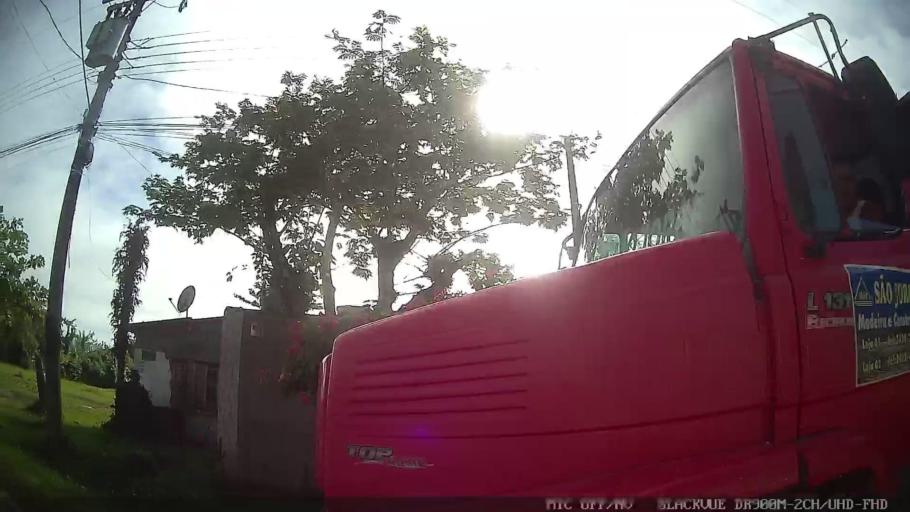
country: BR
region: Sao Paulo
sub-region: Peruibe
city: Peruibe
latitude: -24.2327
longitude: -46.9081
